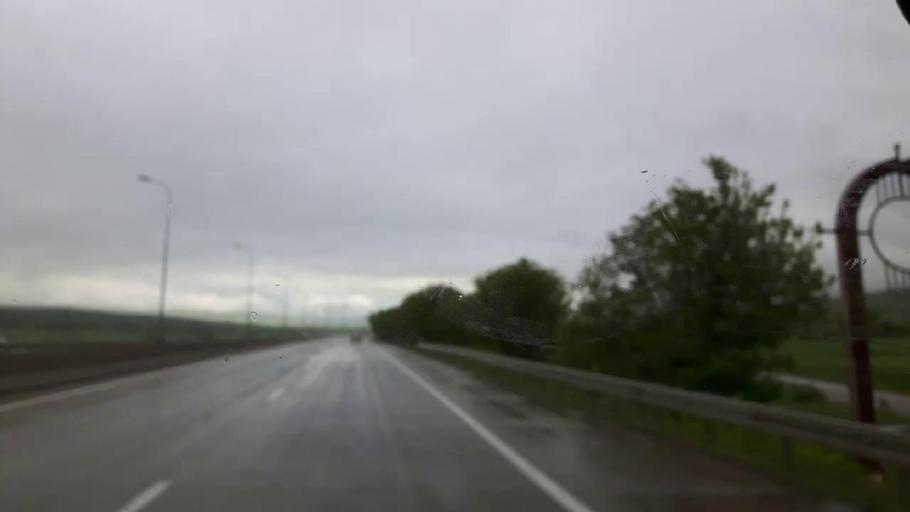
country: GE
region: Shida Kartli
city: Kaspi
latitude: 42.0182
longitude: 44.3141
